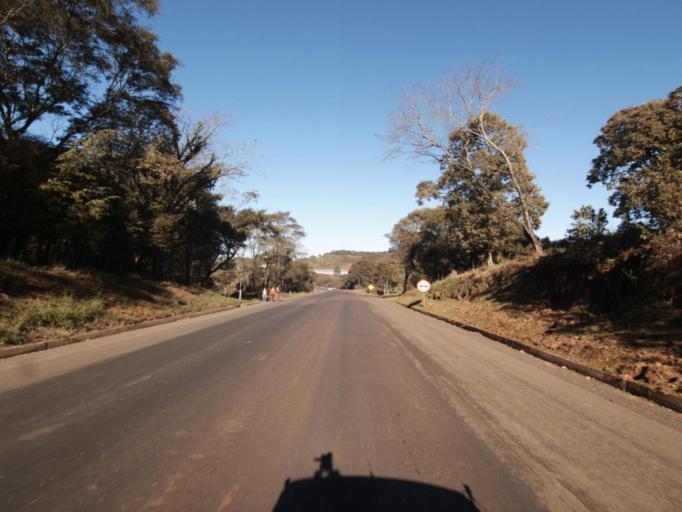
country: BR
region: Rio Grande do Sul
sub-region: Frederico Westphalen
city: Frederico Westphalen
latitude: -26.8927
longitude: -53.1875
